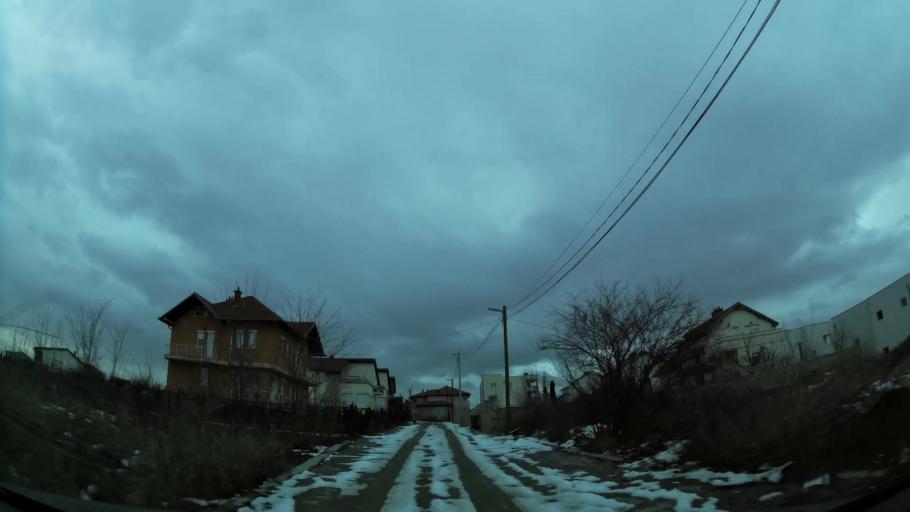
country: XK
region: Pristina
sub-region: Komuna e Prishtines
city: Pristina
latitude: 42.6253
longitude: 21.1652
